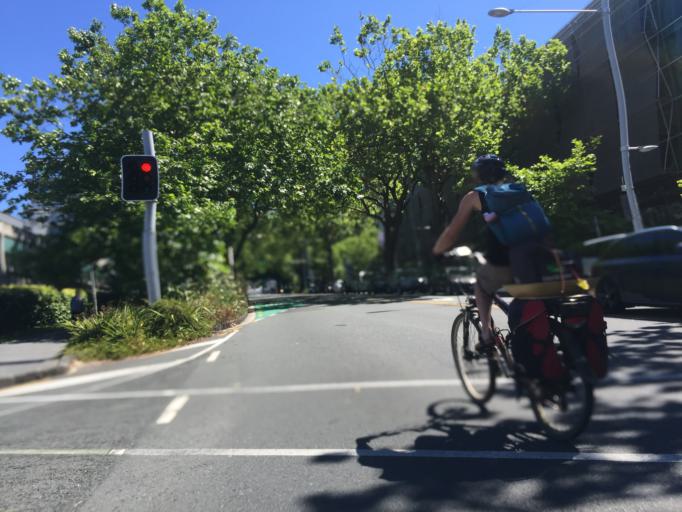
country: NZ
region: Auckland
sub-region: Auckland
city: Auckland
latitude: -36.8519
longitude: 174.7703
